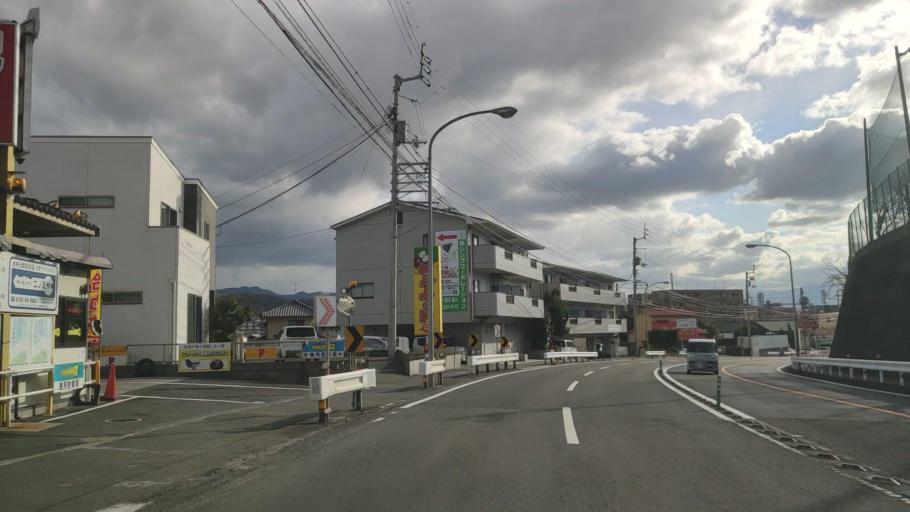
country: JP
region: Ehime
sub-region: Shikoku-chuo Shi
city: Matsuyama
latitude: 33.8575
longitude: 132.7409
